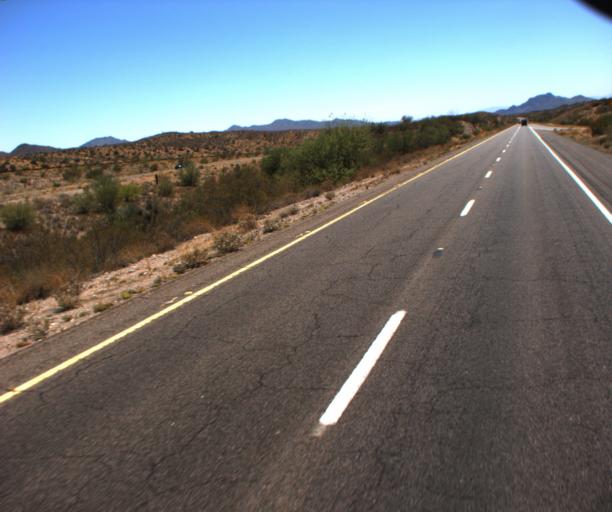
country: US
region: Arizona
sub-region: Maricopa County
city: Rio Verde
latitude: 33.6271
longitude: -111.5605
